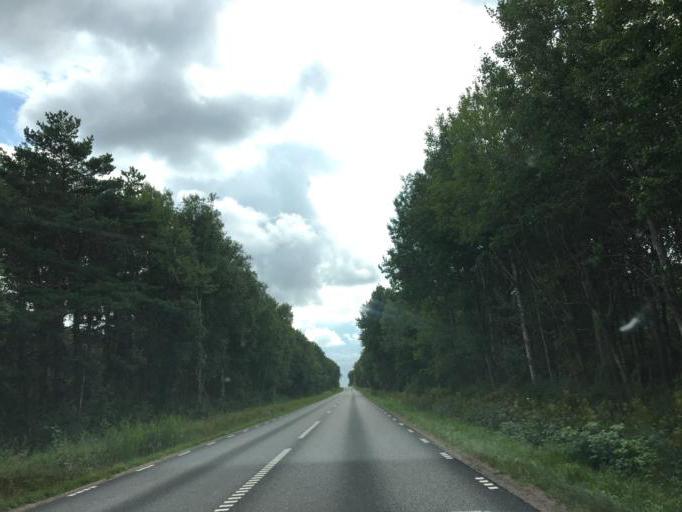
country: SE
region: Vaestra Goetaland
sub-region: Sotenas Kommun
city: Kungshamn
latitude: 58.4033
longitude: 11.2675
